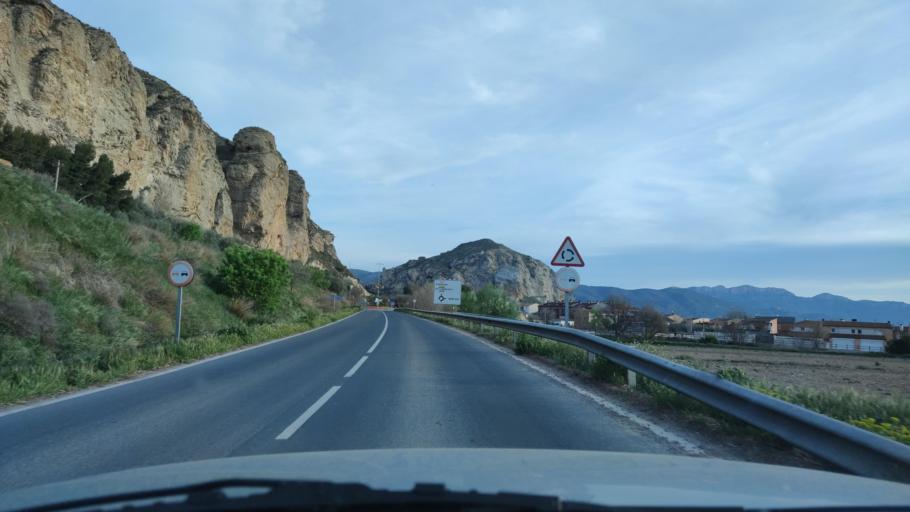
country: ES
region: Catalonia
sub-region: Provincia de Lleida
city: Balaguer
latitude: 41.8181
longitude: 0.8041
